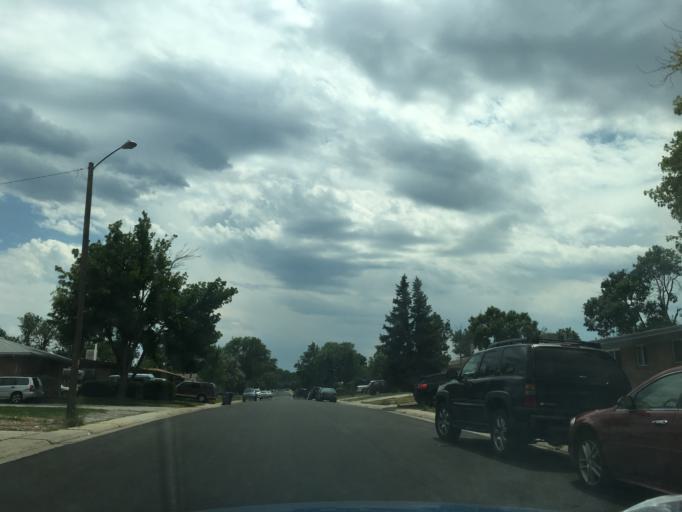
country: US
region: Colorado
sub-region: Jefferson County
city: Lakewood
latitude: 39.6816
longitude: -105.0522
